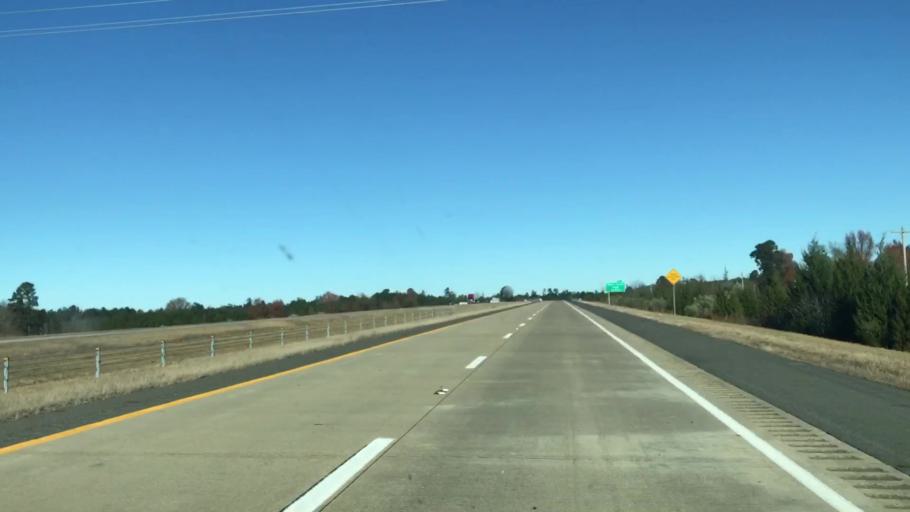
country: US
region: Texas
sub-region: Bowie County
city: Texarkana
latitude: 33.2555
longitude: -93.8940
